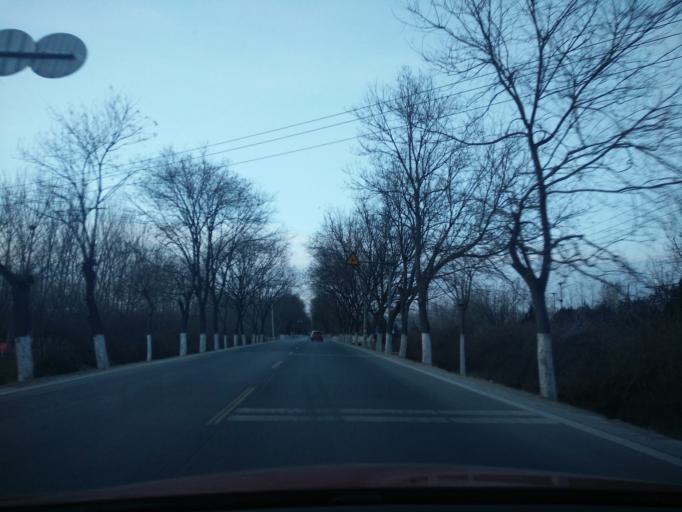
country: CN
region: Beijing
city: Qingyundian
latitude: 39.6814
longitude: 116.4964
